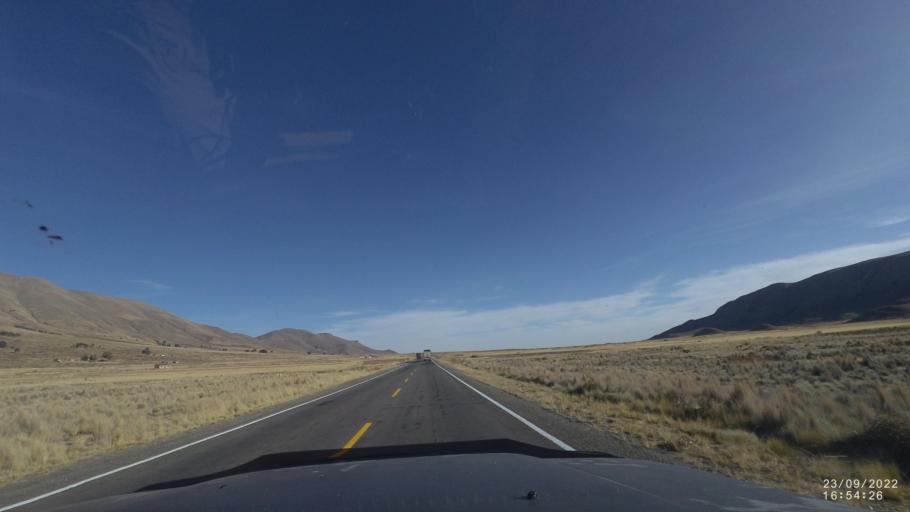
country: BO
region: Oruro
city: Poopo
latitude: -18.4637
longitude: -66.9693
